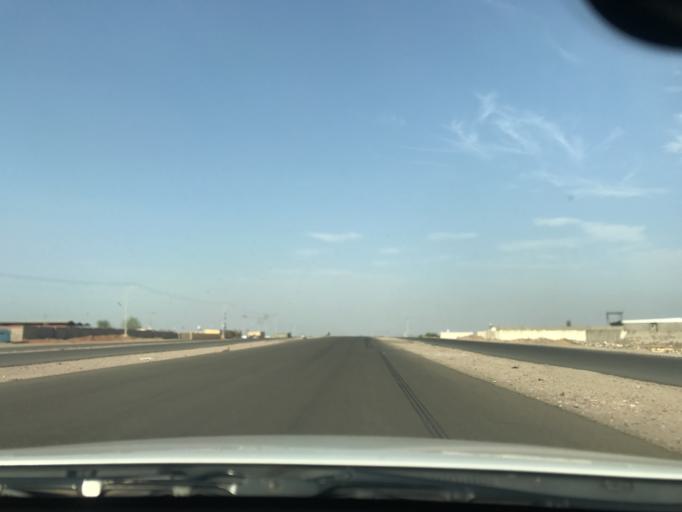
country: SA
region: Makkah
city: Al Jumum
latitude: 21.4529
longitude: 39.5319
